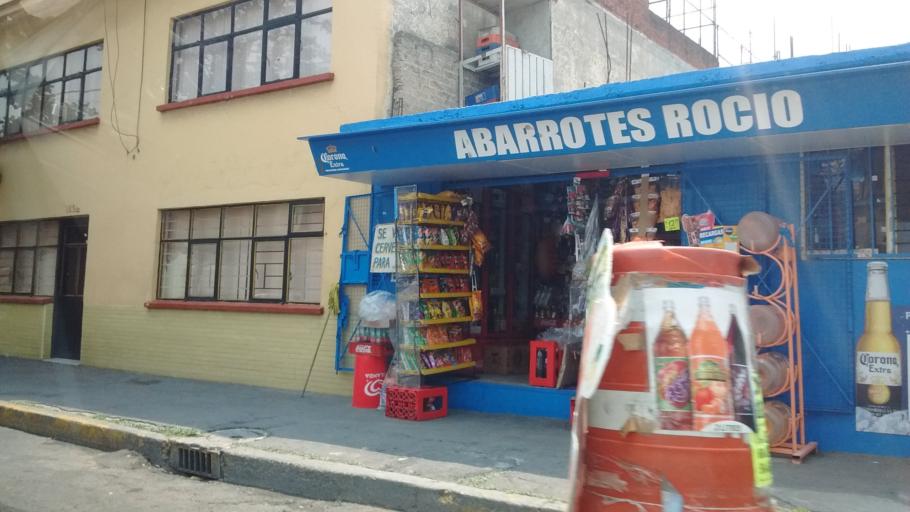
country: MX
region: Mexico City
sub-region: Iztacalco
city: Iztacalco
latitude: 19.4096
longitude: -99.0927
